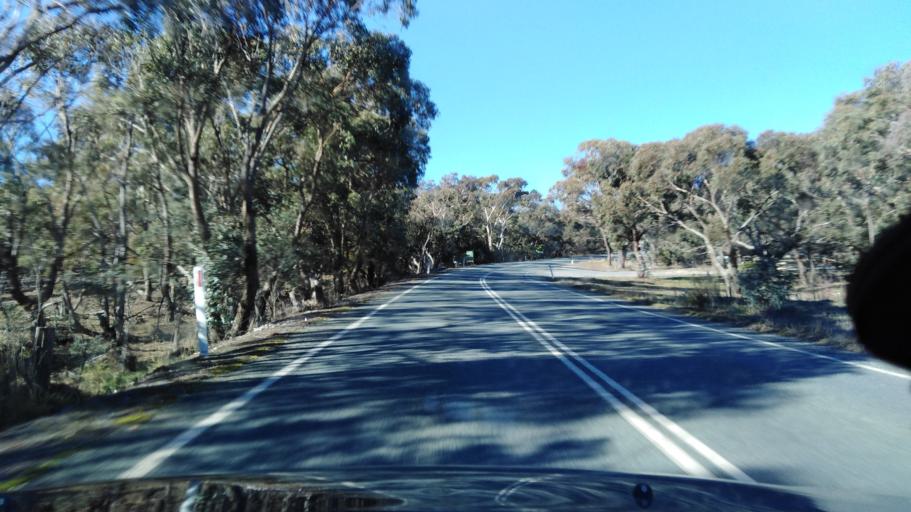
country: AU
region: New South Wales
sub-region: Palerang
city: Bungendore
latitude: -35.2007
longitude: 149.3445
